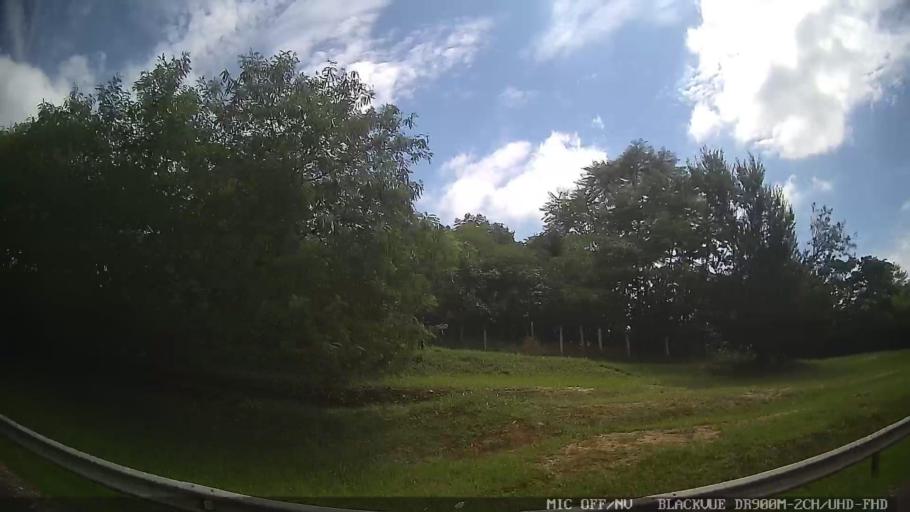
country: BR
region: Sao Paulo
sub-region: Tiete
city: Tiete
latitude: -23.1102
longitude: -47.7482
